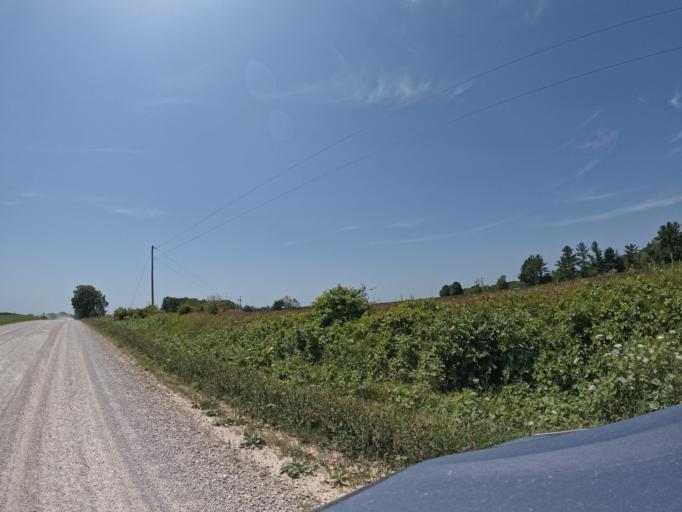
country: US
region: Iowa
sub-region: Henry County
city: Mount Pleasant
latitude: 40.9354
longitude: -91.5831
